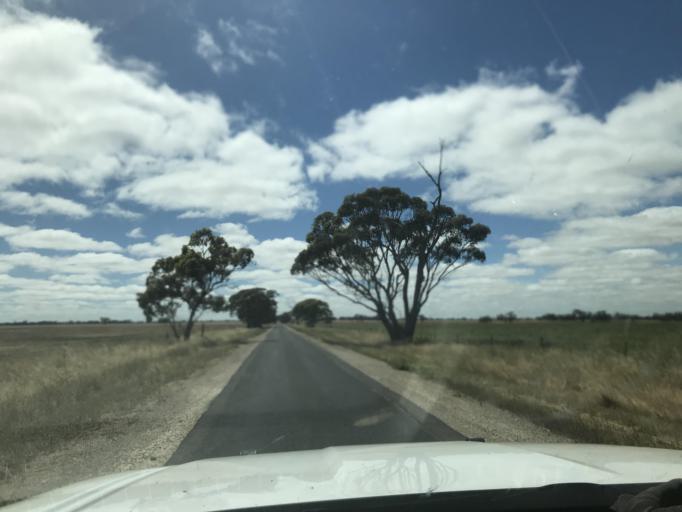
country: AU
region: South Australia
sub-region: Tatiara
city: Bordertown
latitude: -36.2769
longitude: 141.0997
